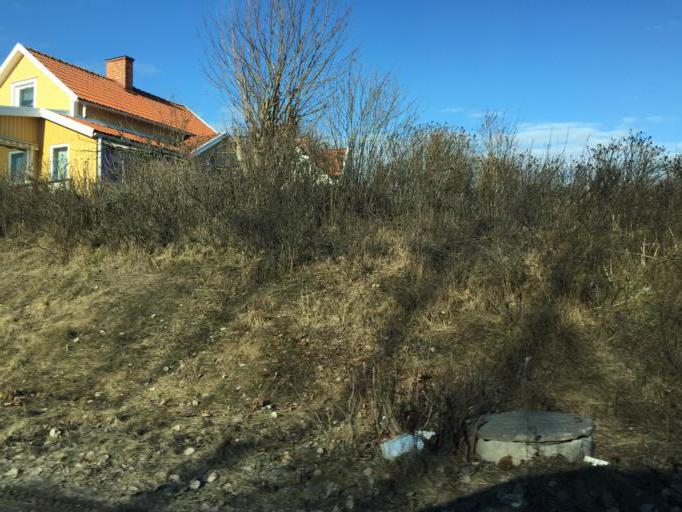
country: SE
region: Soedermanland
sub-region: Vingakers Kommun
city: Vingaker
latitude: 59.0572
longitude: 15.8764
